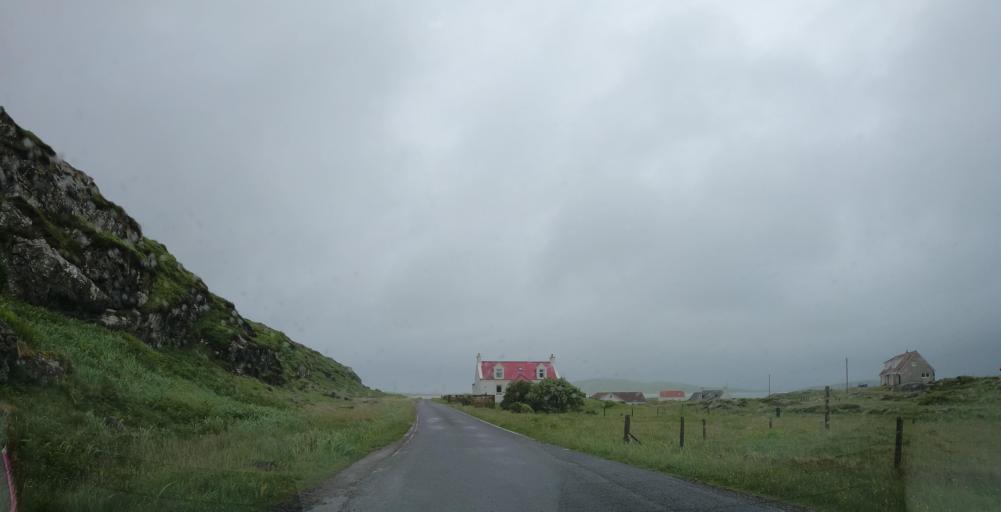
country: GB
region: Scotland
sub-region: Eilean Siar
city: Barra
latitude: 57.0138
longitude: -7.4308
